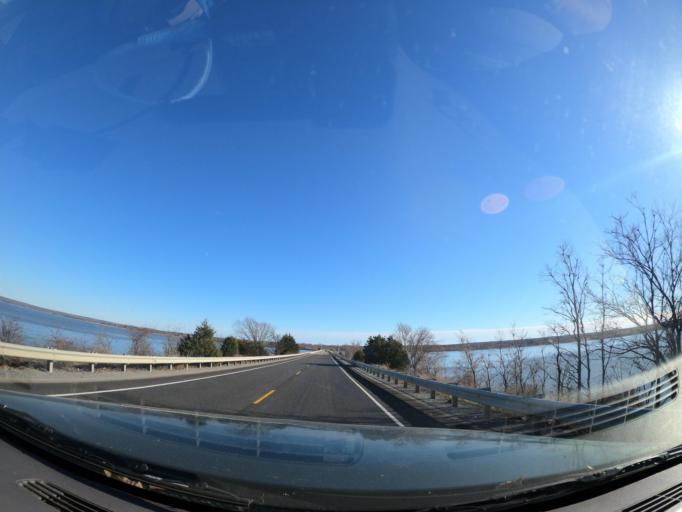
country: US
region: Oklahoma
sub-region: McIntosh County
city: Eufaula
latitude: 35.2471
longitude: -95.5665
